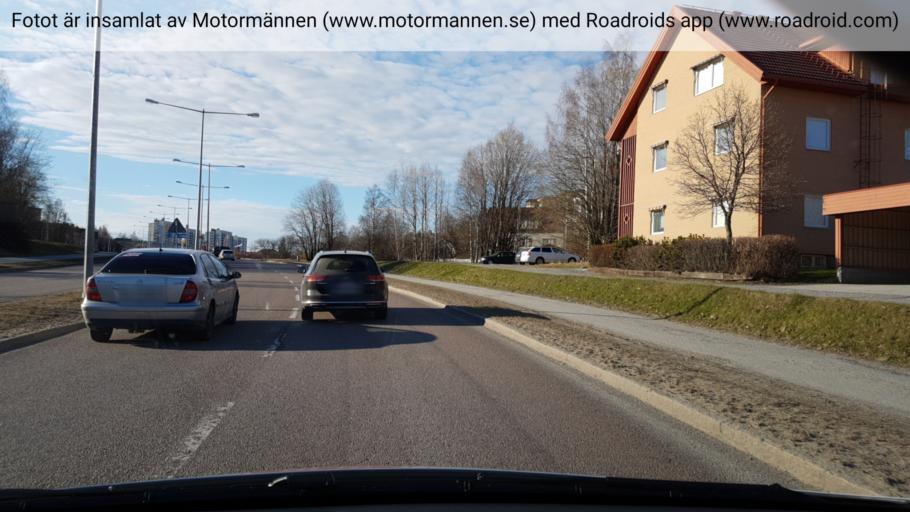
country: SE
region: Vaesternorrland
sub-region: OErnskoeldsviks Kommun
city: Ornskoldsvik
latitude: 63.2933
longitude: 18.7217
